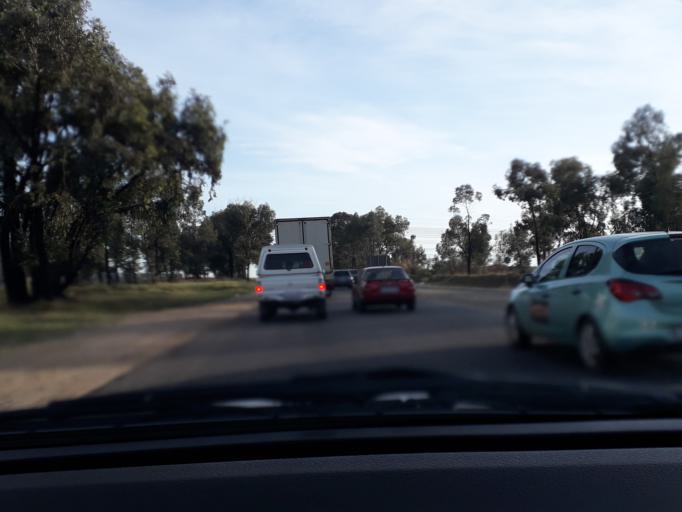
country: ZA
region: Gauteng
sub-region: City of Johannesburg Metropolitan Municipality
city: Midrand
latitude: -25.9245
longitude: 28.1520
